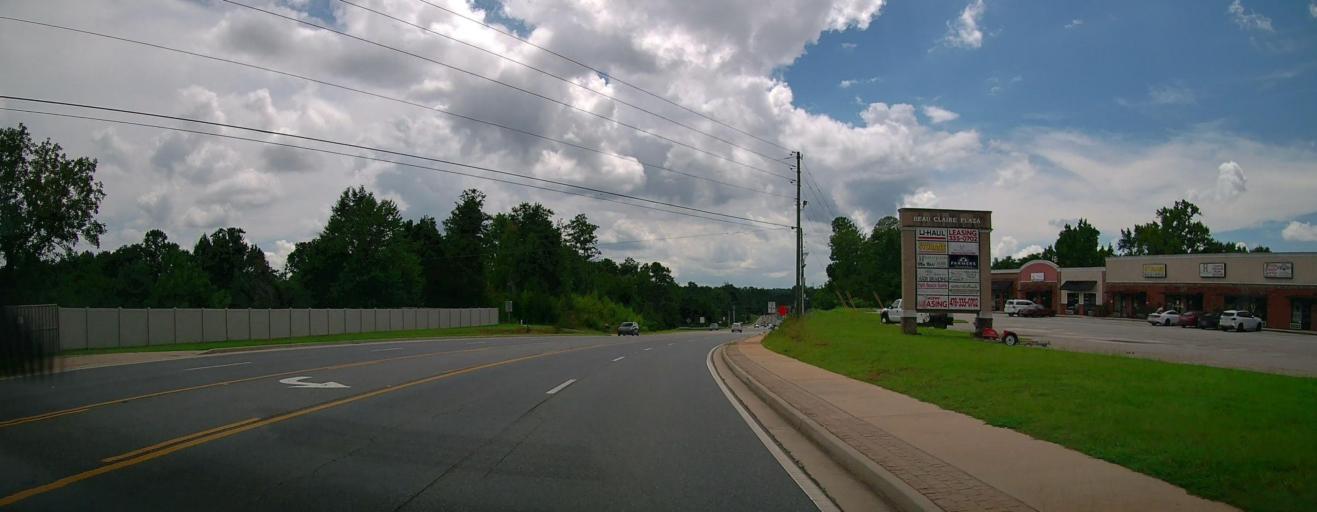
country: US
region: Georgia
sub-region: Houston County
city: Centerville
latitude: 32.6187
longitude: -83.7092
